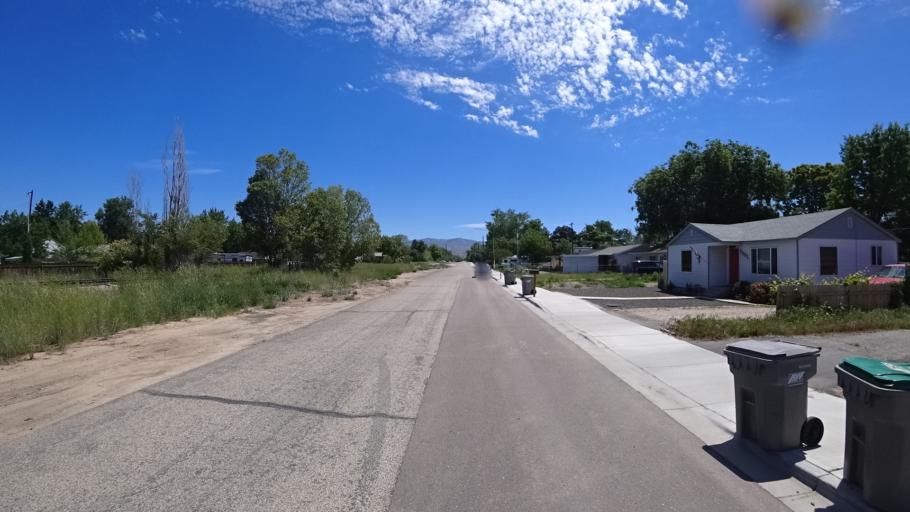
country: US
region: Idaho
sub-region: Ada County
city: Garden City
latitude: 43.6044
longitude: -116.2414
